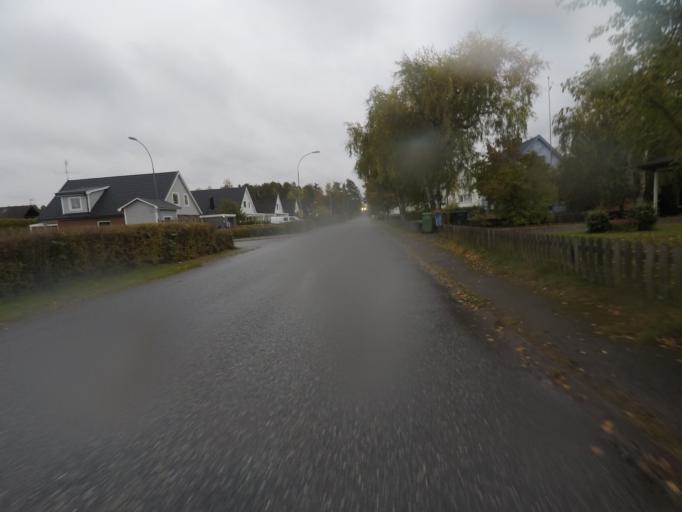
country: SE
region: OErebro
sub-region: Karlskoga Kommun
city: Karlskoga
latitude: 59.3084
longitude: 14.4832
